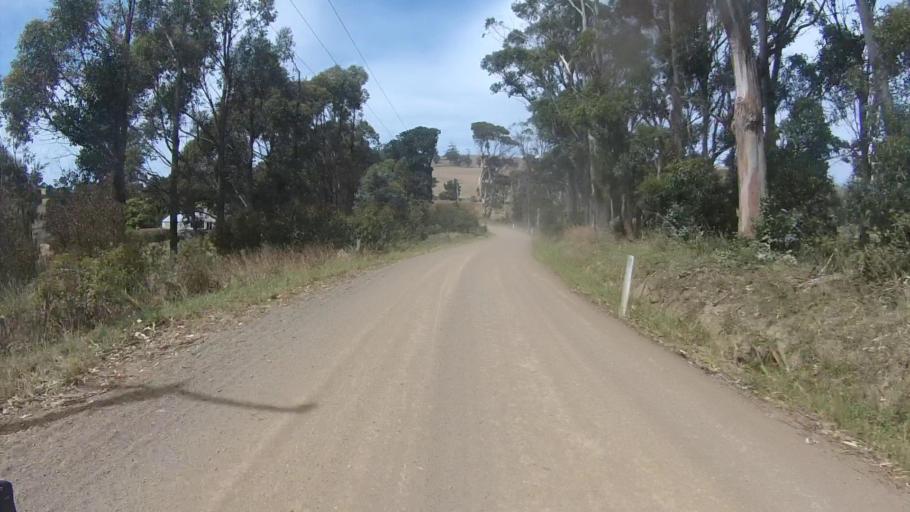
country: AU
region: Tasmania
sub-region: Sorell
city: Sorell
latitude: -42.8193
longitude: 147.8239
